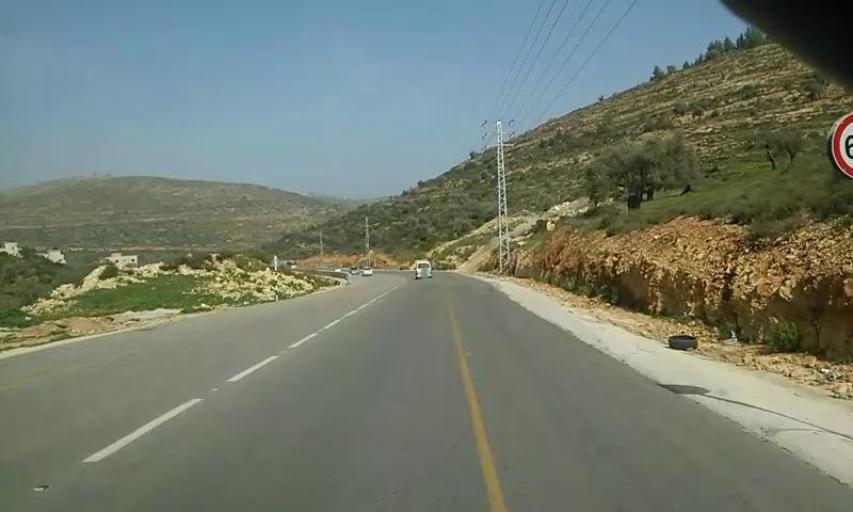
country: PS
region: West Bank
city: Dura al Qar`
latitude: 31.9835
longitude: 35.2329
